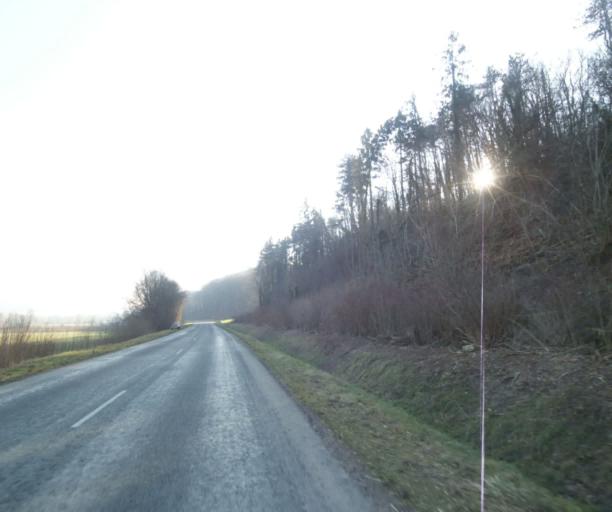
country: FR
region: Champagne-Ardenne
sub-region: Departement de la Haute-Marne
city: Chevillon
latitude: 48.4992
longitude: 5.1193
